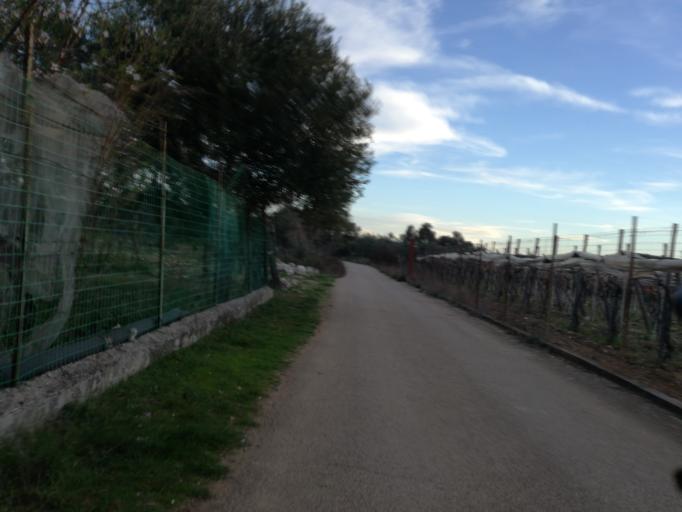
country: IT
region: Apulia
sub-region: Provincia di Bari
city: Lamie
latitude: 41.0238
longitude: 16.8718
